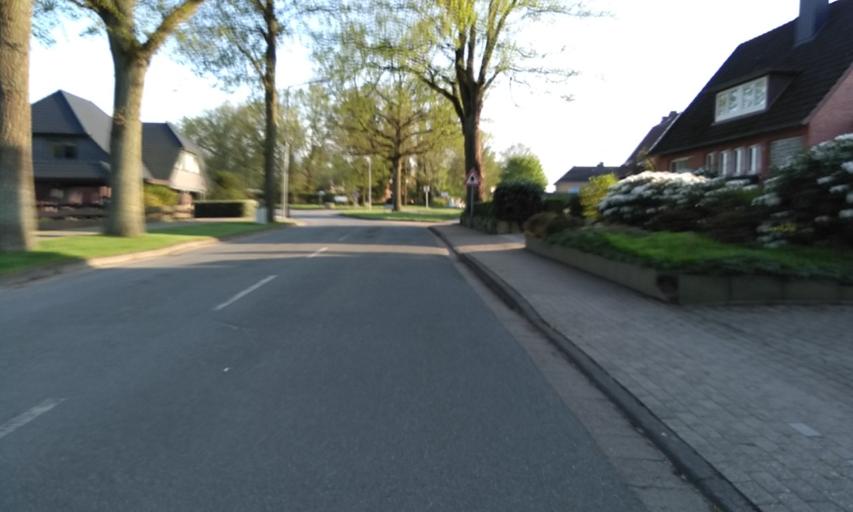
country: DE
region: Lower Saxony
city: Dollern
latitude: 53.5357
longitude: 9.5477
